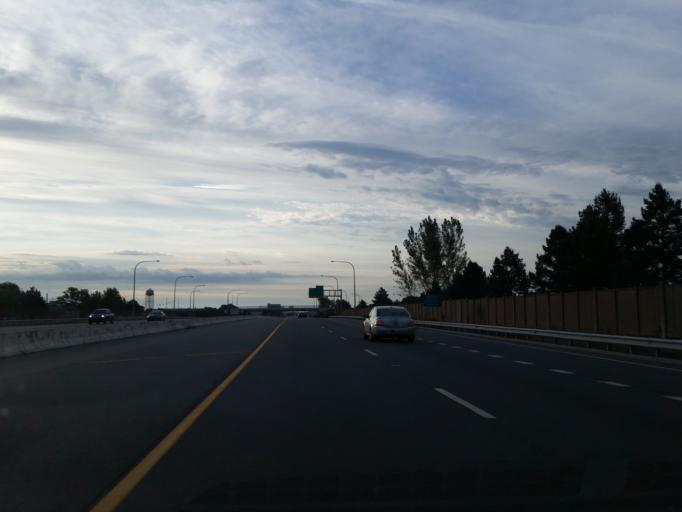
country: US
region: Delaware
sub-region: Kent County
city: Dover Base Housing
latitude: 39.1244
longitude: -75.4854
